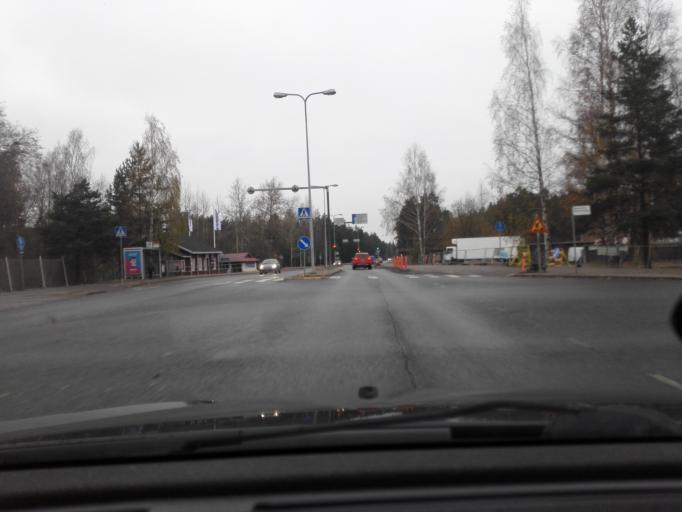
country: FI
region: Uusimaa
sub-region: Helsinki
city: Vantaa
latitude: 60.2862
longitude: 25.0806
